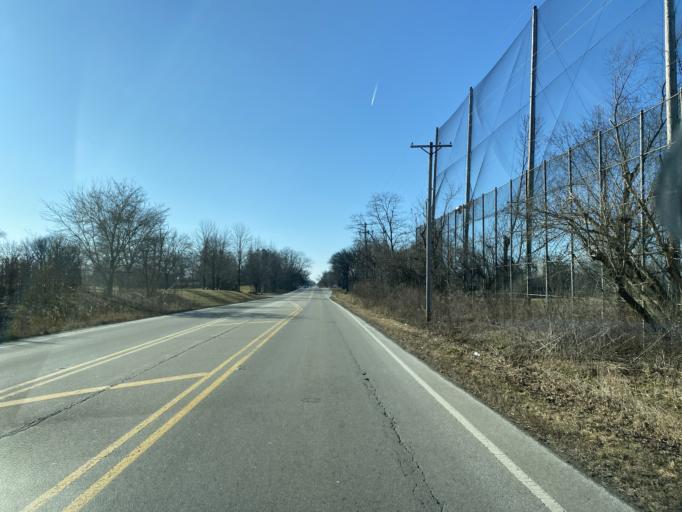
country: US
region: Illinois
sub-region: Will County
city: Goodings Grove
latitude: 41.6740
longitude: -87.9491
